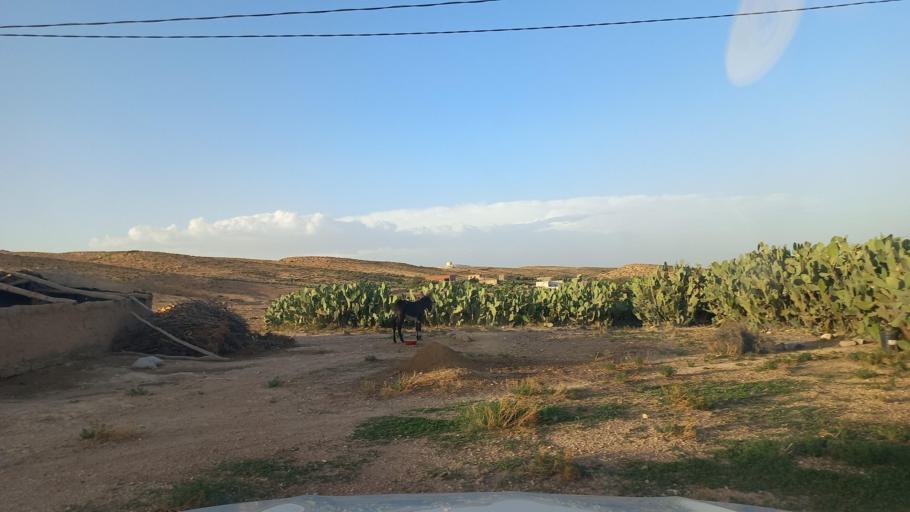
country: TN
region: Al Qasrayn
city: Sbiba
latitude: 35.3722
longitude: 9.0025
